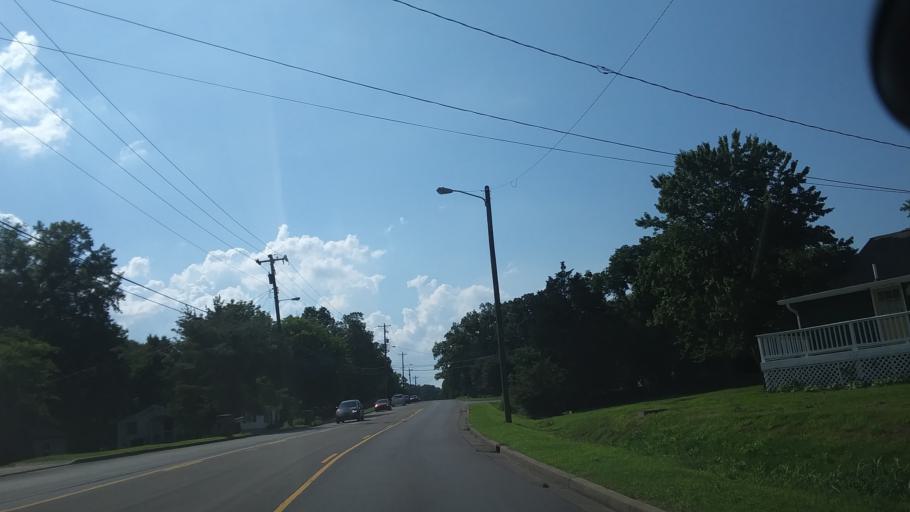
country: US
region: Tennessee
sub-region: Rutherford County
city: La Vergne
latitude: 36.0913
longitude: -86.6297
